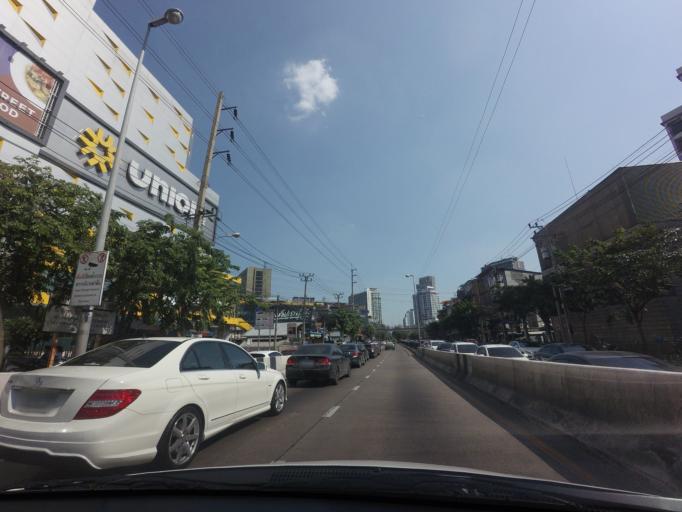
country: TH
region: Bangkok
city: Chatuchak
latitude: 13.8127
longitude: 100.5619
